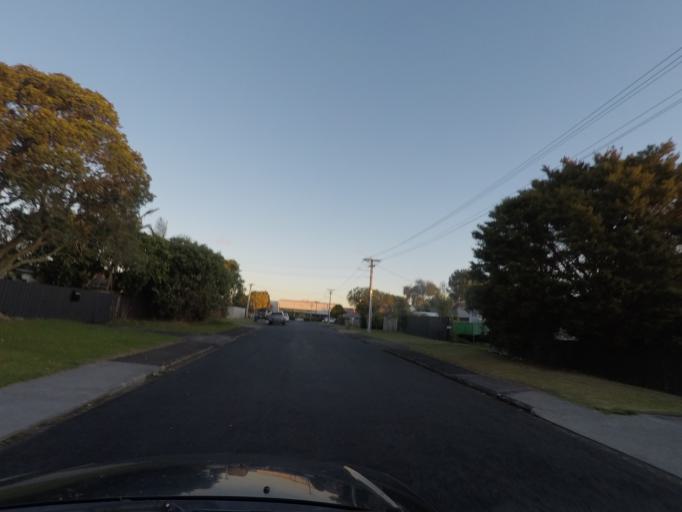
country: NZ
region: Auckland
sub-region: Auckland
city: Rosebank
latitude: -36.8274
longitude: 174.6491
